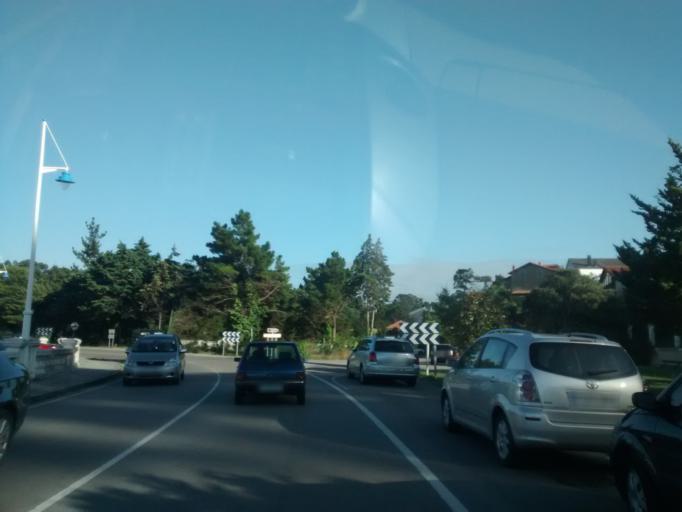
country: ES
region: Cantabria
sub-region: Provincia de Cantabria
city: Santander
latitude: 43.4464
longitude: -3.7662
